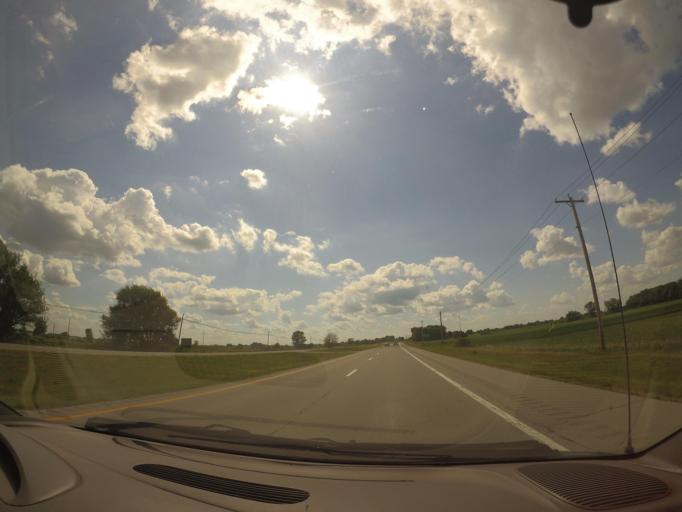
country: US
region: Ohio
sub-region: Huron County
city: Bellevue
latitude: 41.2658
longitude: -82.7999
